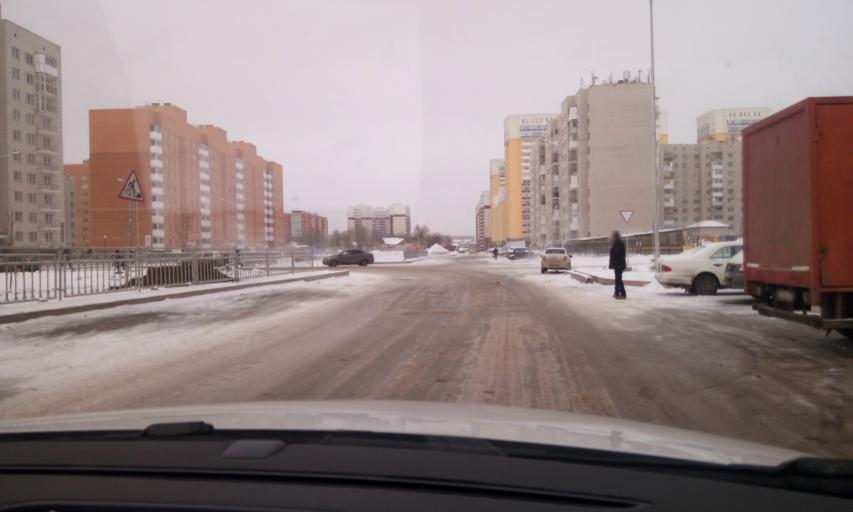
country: KZ
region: Astana Qalasy
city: Astana
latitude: 51.1259
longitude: 71.5049
